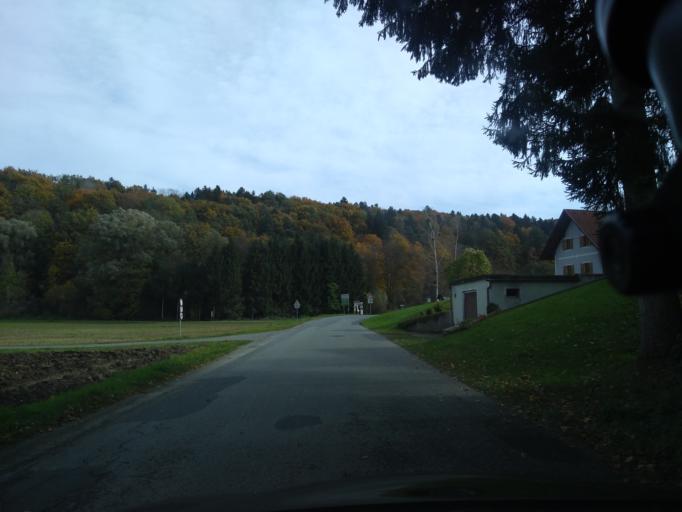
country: AT
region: Styria
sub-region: Politischer Bezirk Leibnitz
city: Heimschuh
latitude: 46.7567
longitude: 15.5011
